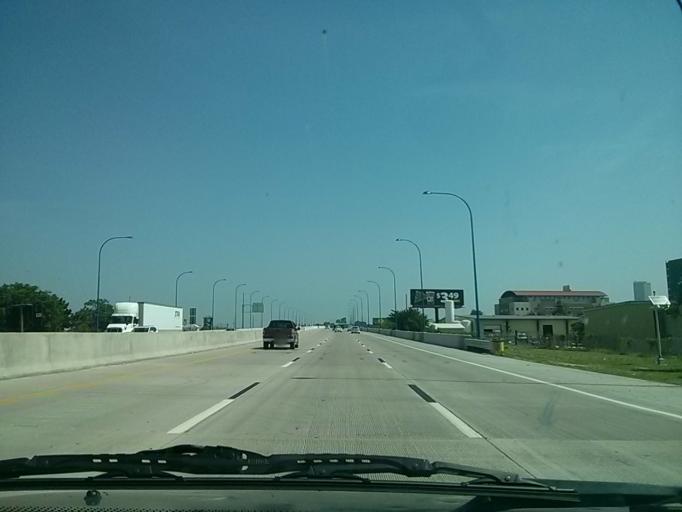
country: US
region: Oklahoma
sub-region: Tulsa County
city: Tulsa
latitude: 36.1341
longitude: -96.0082
